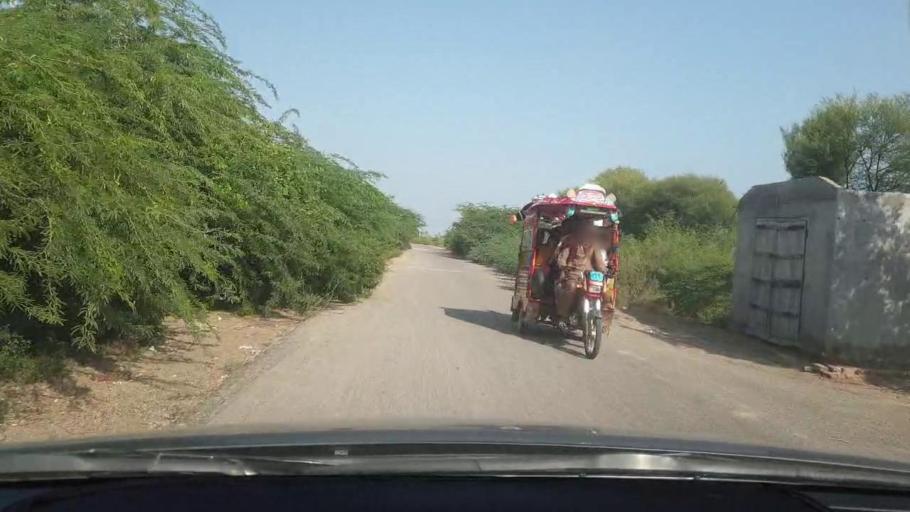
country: PK
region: Sindh
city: Naukot
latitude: 24.7610
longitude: 69.2239
